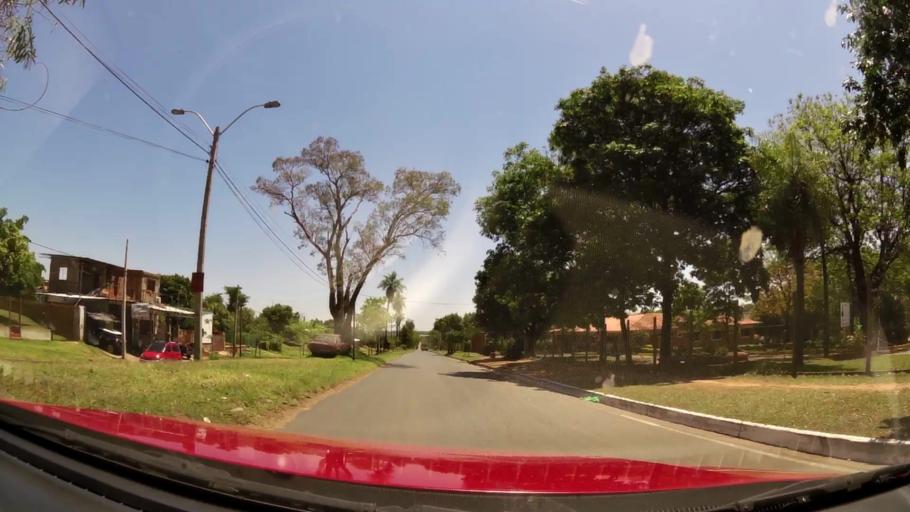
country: PY
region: Central
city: Colonia Mariano Roque Alonso
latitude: -25.2311
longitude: -57.5534
